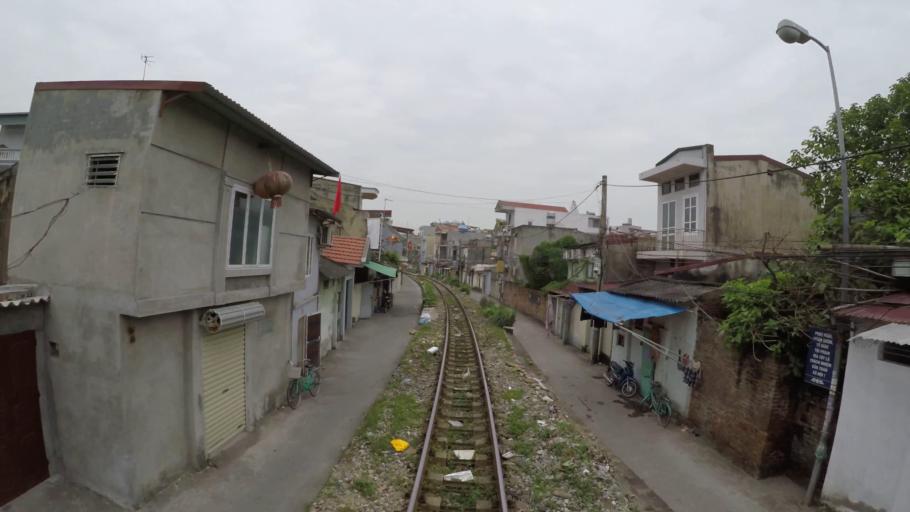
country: VN
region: Hai Phong
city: Haiphong
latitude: 20.8680
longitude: 106.6554
